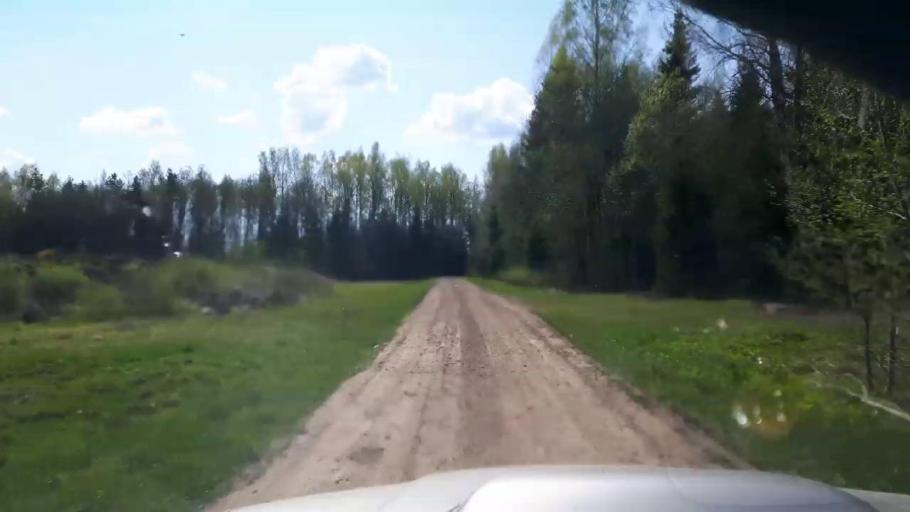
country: EE
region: Paernumaa
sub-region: Tootsi vald
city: Tootsi
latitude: 58.4967
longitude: 24.9425
